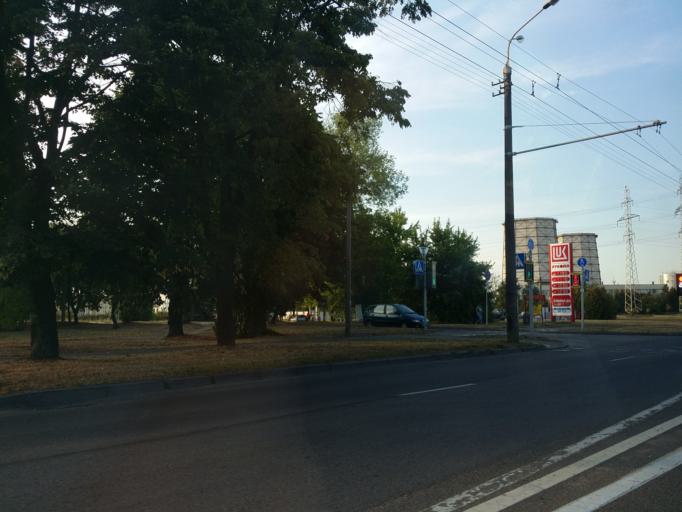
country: BY
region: Minsk
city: Vyaliki Trastsyanets
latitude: 53.8753
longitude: 27.6522
